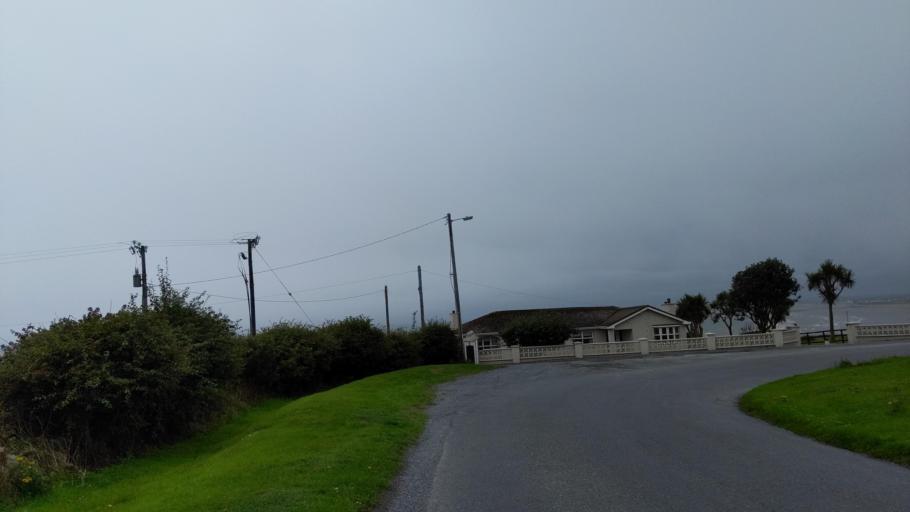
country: IE
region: Leinster
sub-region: Lu
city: Clogherhead
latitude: 53.7922
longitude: -6.2281
